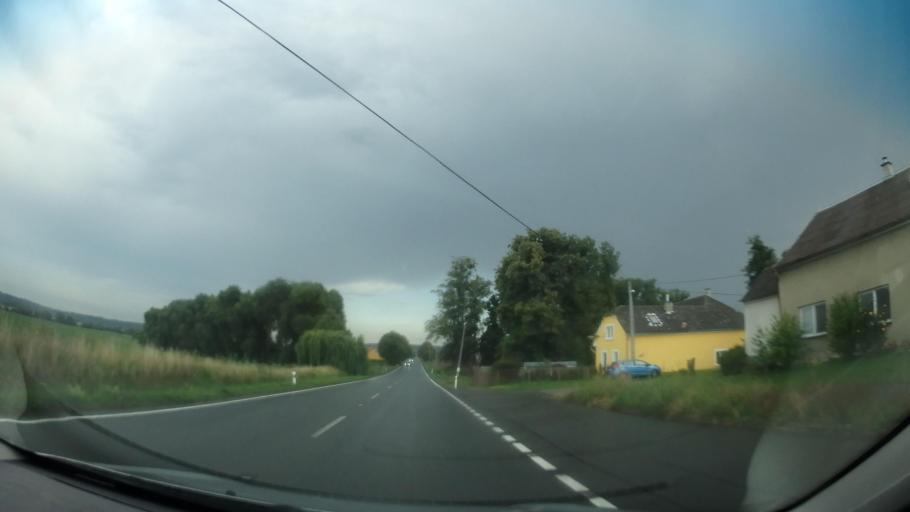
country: CZ
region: Olomoucky
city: Moravicany
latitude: 49.7317
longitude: 16.9568
